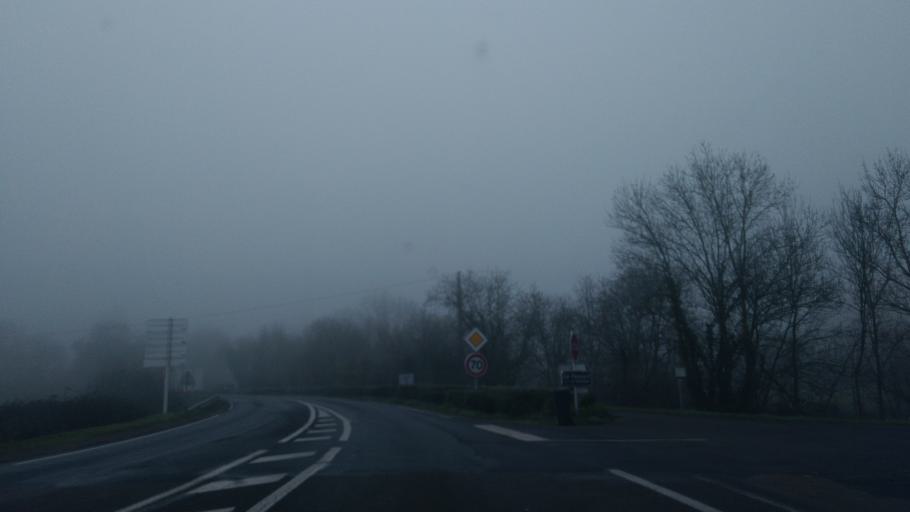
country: FR
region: Pays de la Loire
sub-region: Departement de la Vendee
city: Soullans
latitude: 46.8322
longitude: -1.9219
